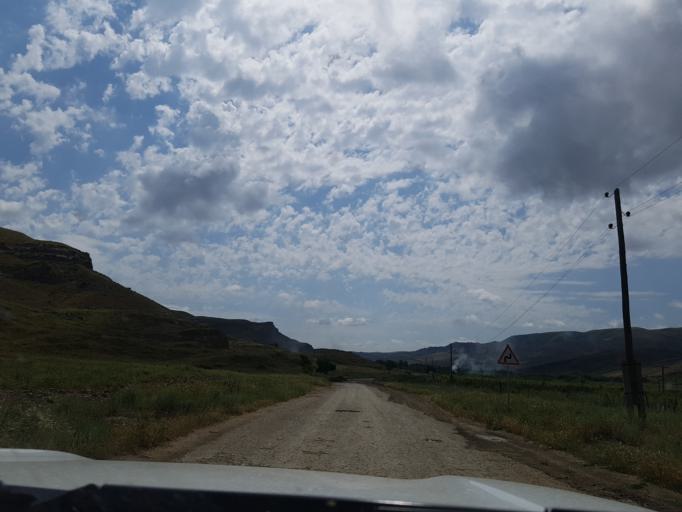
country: TM
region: Ahal
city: Baharly
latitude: 38.2287
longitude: 56.8700
